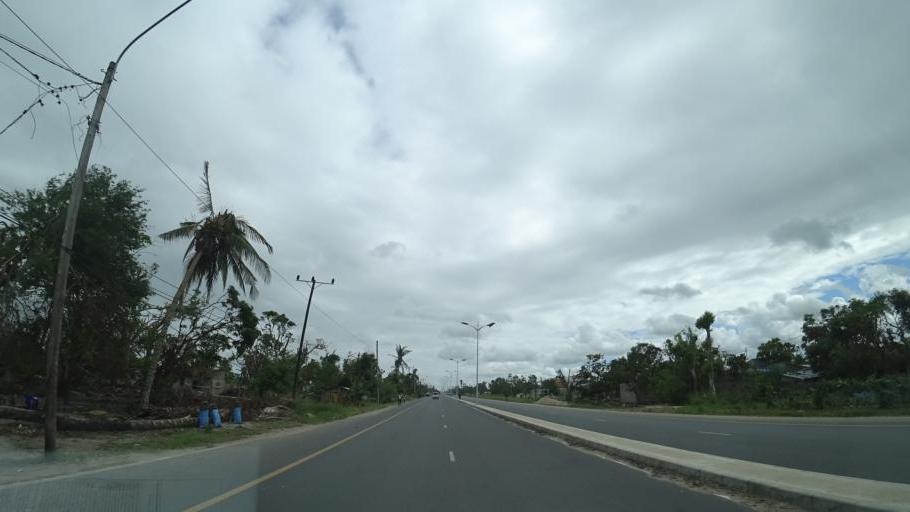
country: MZ
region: Sofala
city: Beira
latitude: -19.7210
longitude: 34.8067
